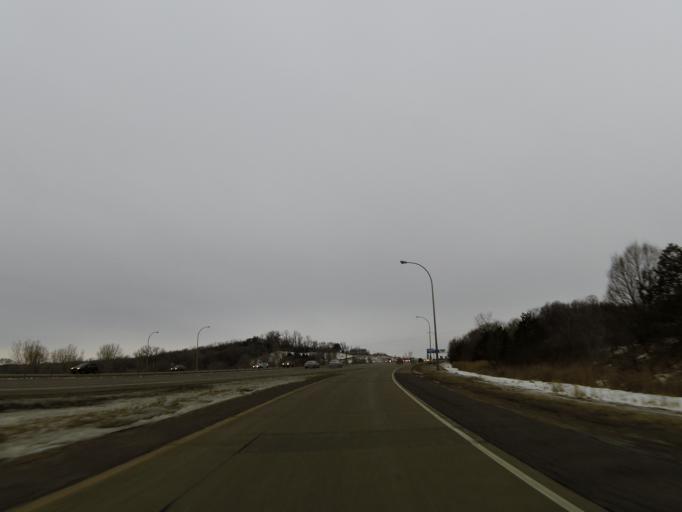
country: US
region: Minnesota
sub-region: Washington County
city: Lakeland
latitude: 44.9616
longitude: -92.7765
